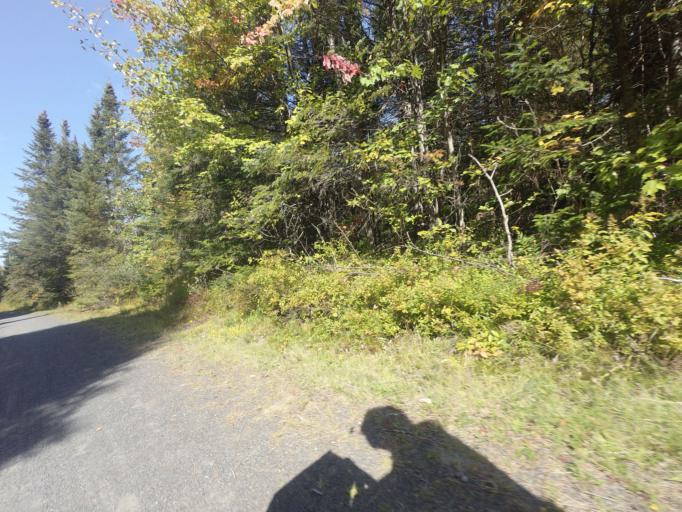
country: CA
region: Quebec
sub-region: Laurentides
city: Sainte-Agathe-des-Monts
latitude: 46.0597
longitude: -74.2882
